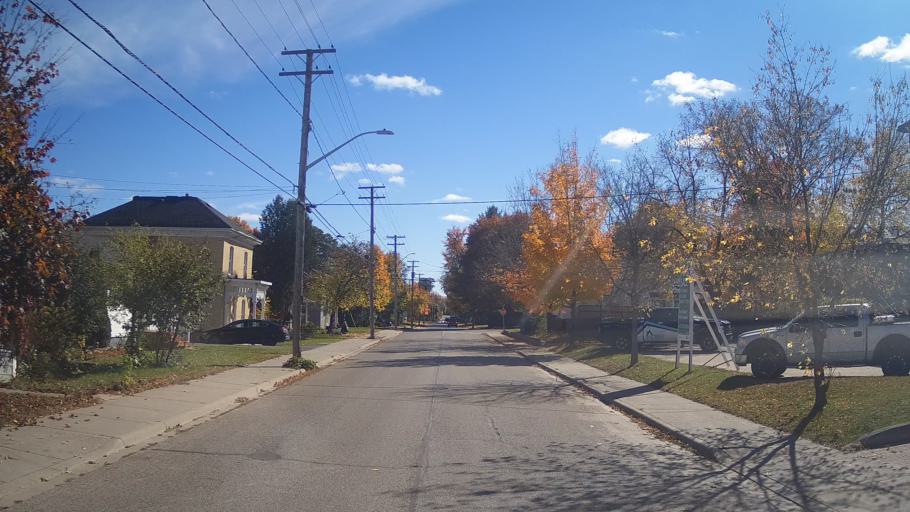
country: CA
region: Ontario
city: Perth
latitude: 44.8991
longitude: -76.2438
